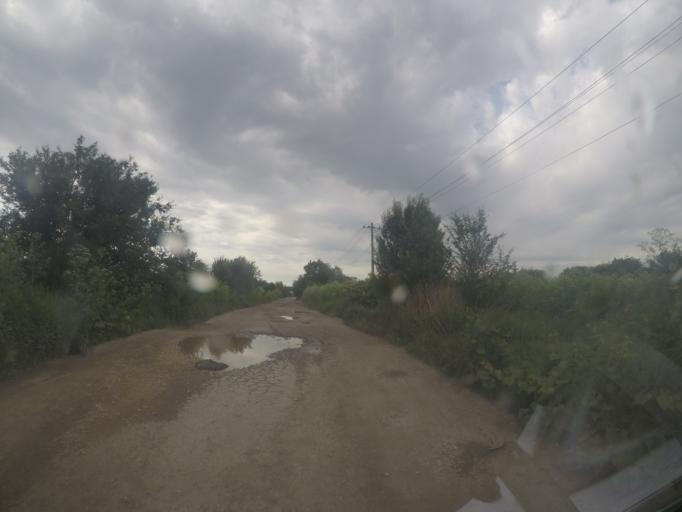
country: RS
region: Central Serbia
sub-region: Belgrade
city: Zemun
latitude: 44.8820
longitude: 20.3835
